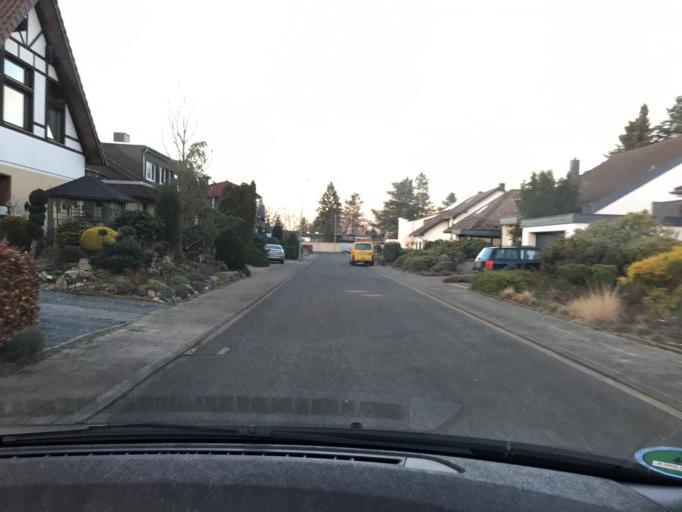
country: DE
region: North Rhine-Westphalia
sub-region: Regierungsbezirk Koln
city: Kreuzau
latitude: 50.7752
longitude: 6.4531
